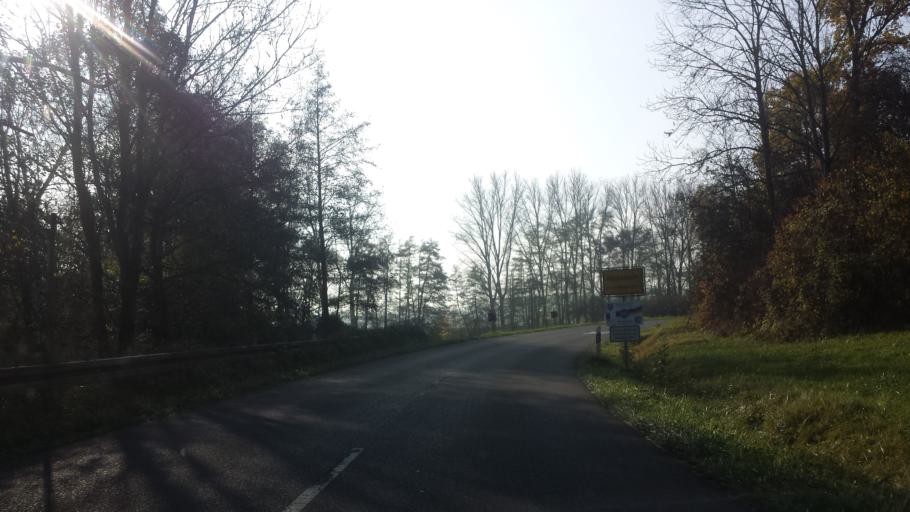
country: DE
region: Baden-Wuerttemberg
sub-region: Karlsruhe Region
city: Meckesheim
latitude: 49.3124
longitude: 8.8288
